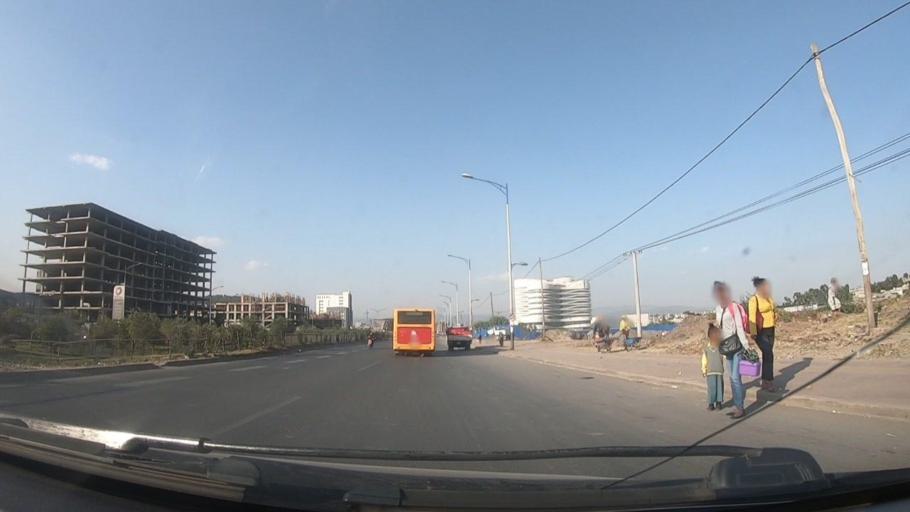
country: ET
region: Adis Abeba
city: Addis Ababa
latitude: 8.9314
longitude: 38.7342
